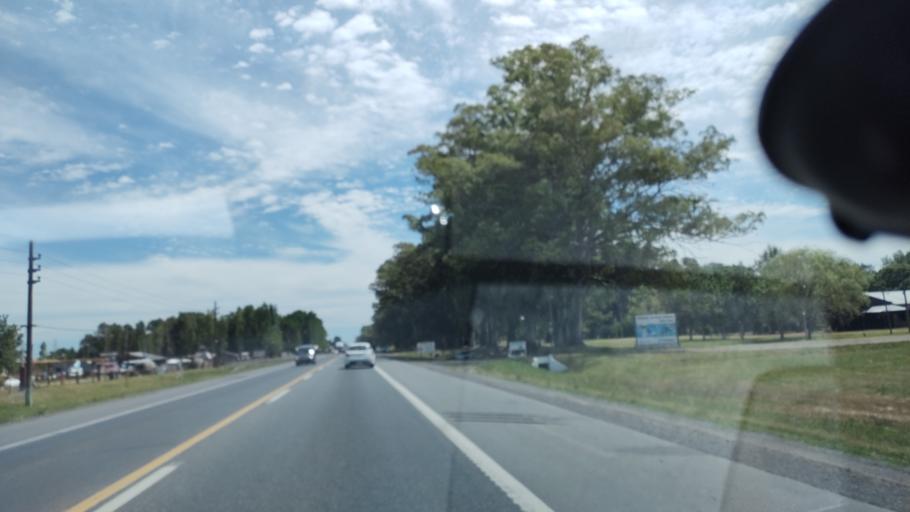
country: AR
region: Buenos Aires
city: Canuelas
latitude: -35.0285
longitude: -58.7475
